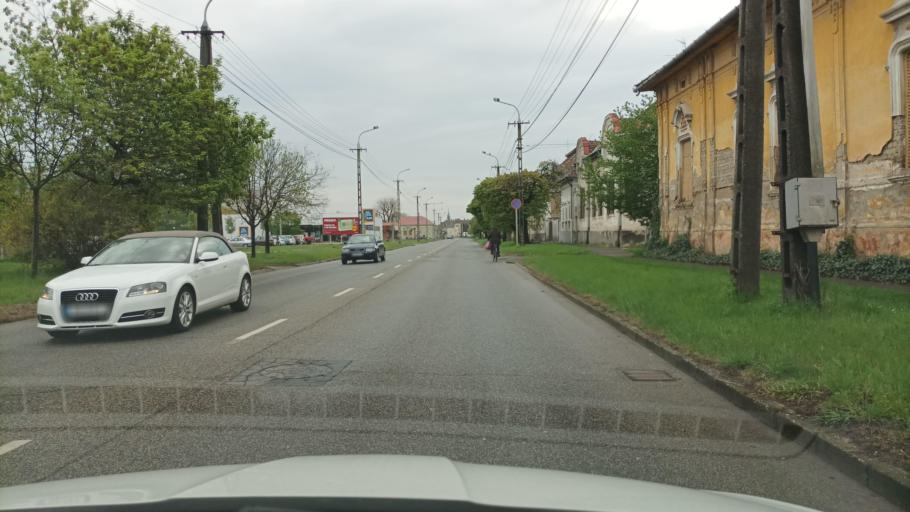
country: HU
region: Pest
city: Nagykoros
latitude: 47.0345
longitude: 19.7663
